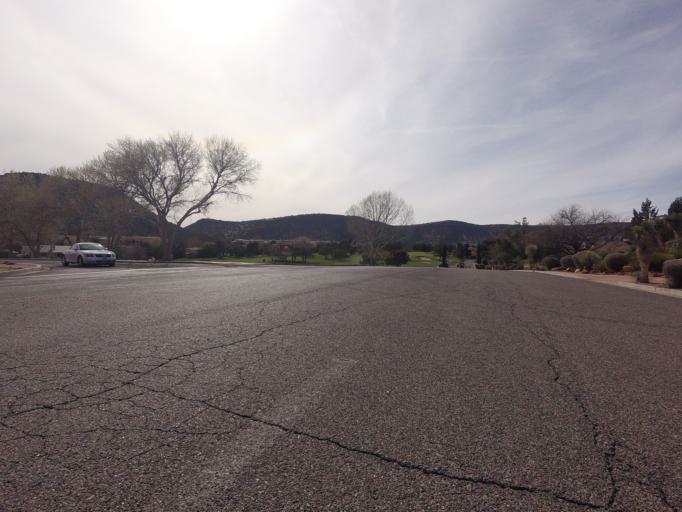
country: US
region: Arizona
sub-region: Yavapai County
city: Big Park
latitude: 34.7737
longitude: -111.7657
